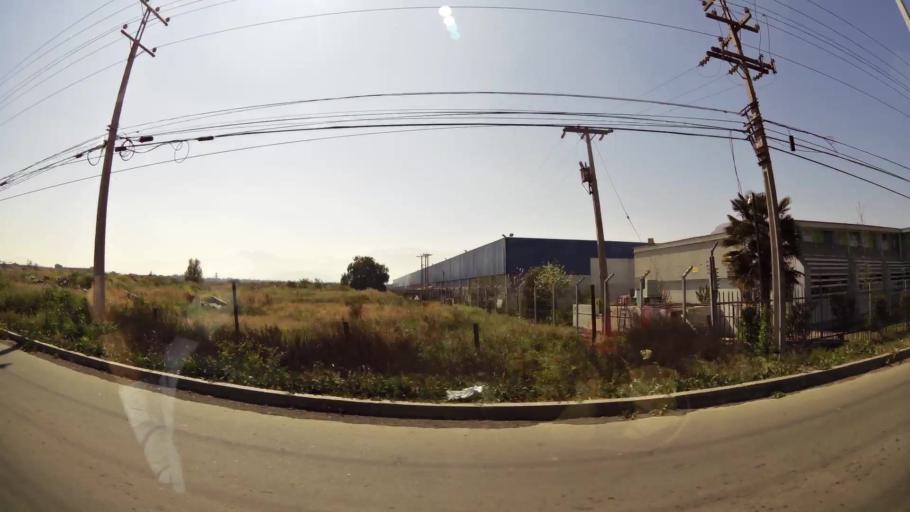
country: CL
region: Santiago Metropolitan
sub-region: Provincia de Chacabuco
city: Chicureo Abajo
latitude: -33.3075
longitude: -70.7261
